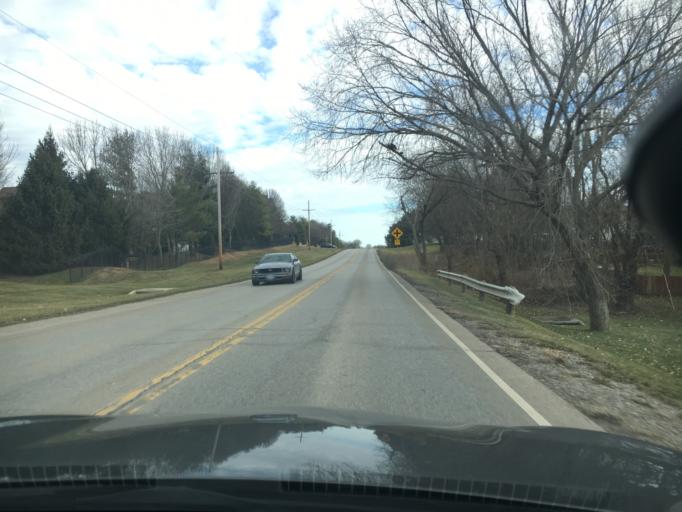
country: US
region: Missouri
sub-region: Jackson County
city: Grandview
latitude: 38.8547
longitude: -94.6405
